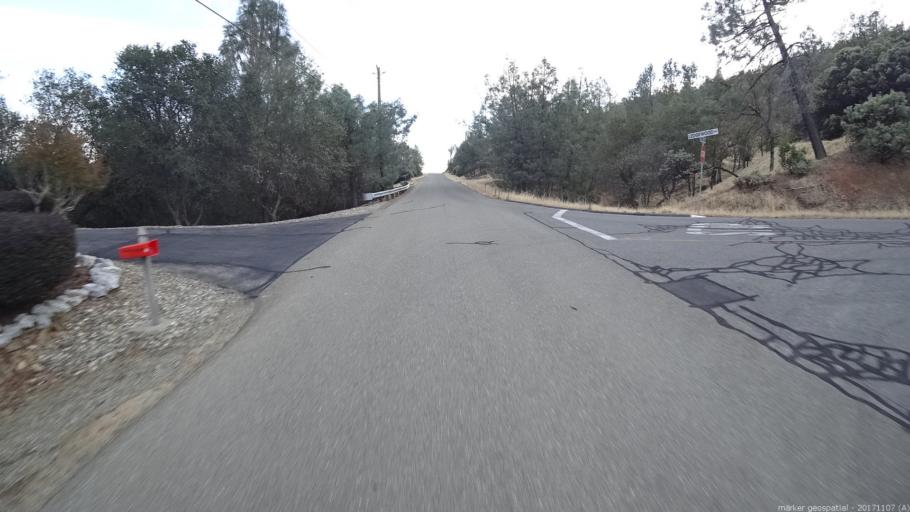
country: US
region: California
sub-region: Shasta County
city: Shasta
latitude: 40.5393
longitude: -122.4913
